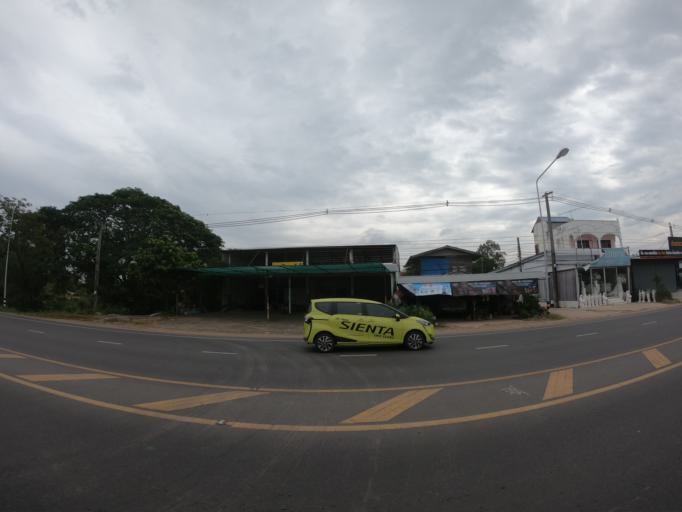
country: TH
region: Roi Et
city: Roi Et
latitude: 16.0749
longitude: 103.6857
